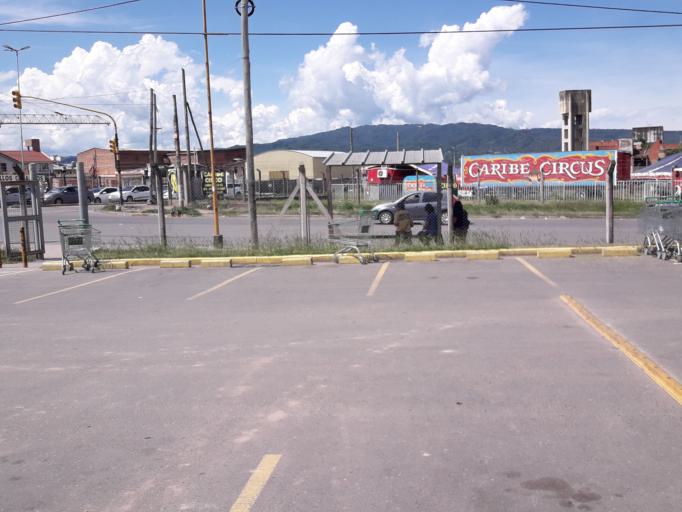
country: AR
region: Jujuy
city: San Salvador de Jujuy
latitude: -24.2102
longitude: -65.2888
